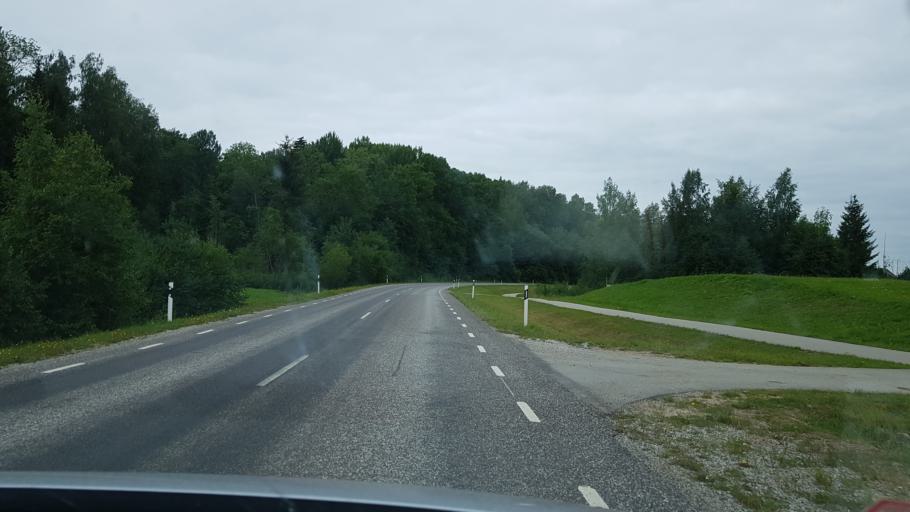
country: EE
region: Vorumaa
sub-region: Antsla vald
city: Vana-Antsla
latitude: 58.0445
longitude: 26.5477
